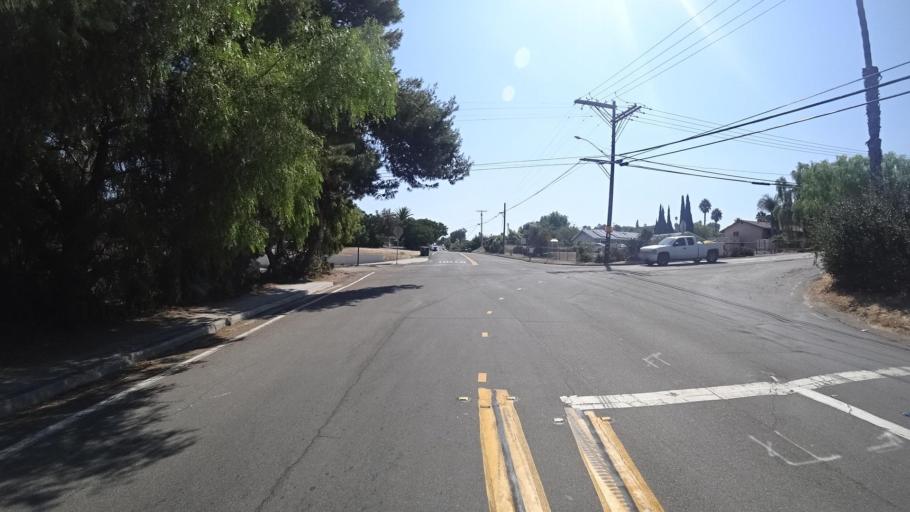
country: US
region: California
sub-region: San Diego County
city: Lake San Marcos
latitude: 33.1531
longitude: -117.2074
